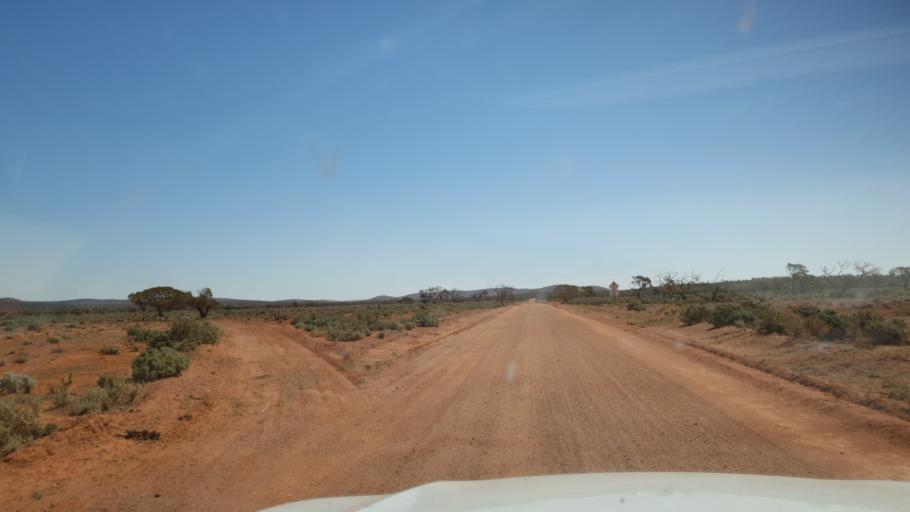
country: AU
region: South Australia
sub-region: Whyalla
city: Whyalla
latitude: -32.6229
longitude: 136.7838
